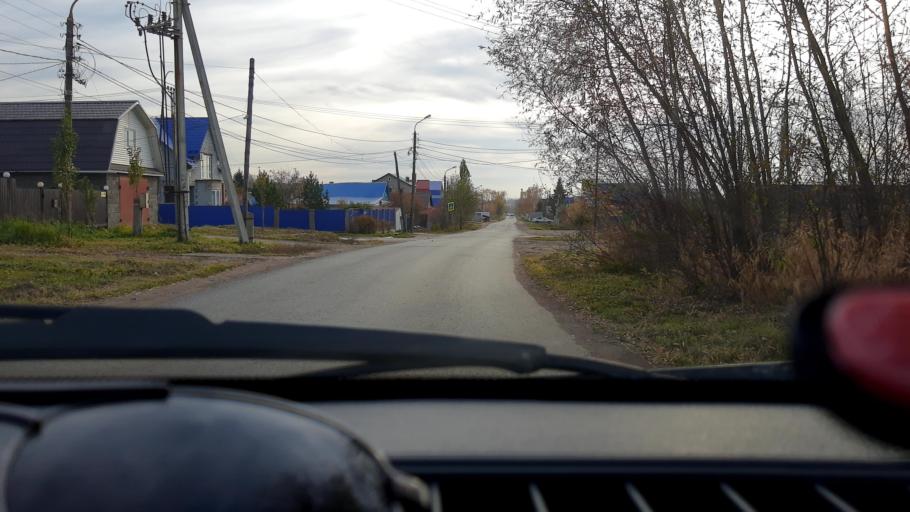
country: RU
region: Bashkortostan
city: Ufa
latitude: 54.8426
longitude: 56.1511
